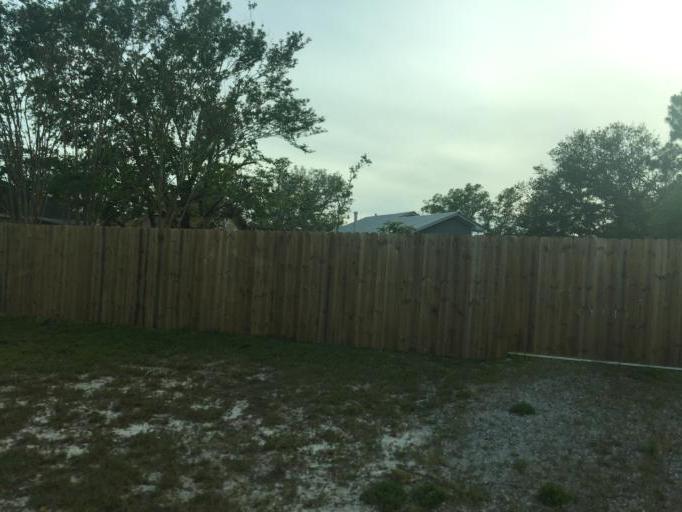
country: US
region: Florida
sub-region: Bay County
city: Lower Grand Lagoon
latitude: 30.1666
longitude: -85.7711
